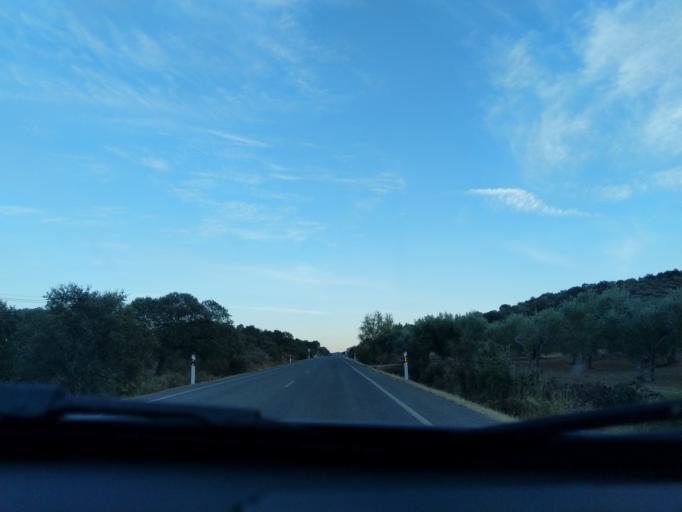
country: ES
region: Extremadura
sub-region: Provincia de Badajoz
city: Reina
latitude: 38.1808
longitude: -5.9296
